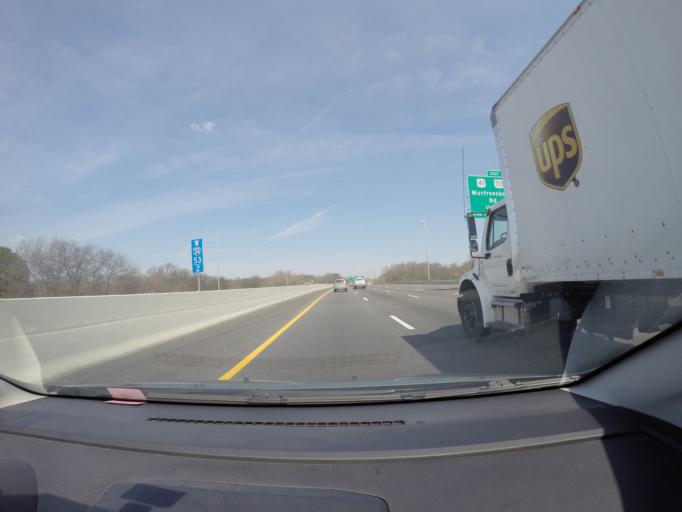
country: US
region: Tennessee
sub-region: Davidson County
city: Oak Hill
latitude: 36.1158
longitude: -86.7250
